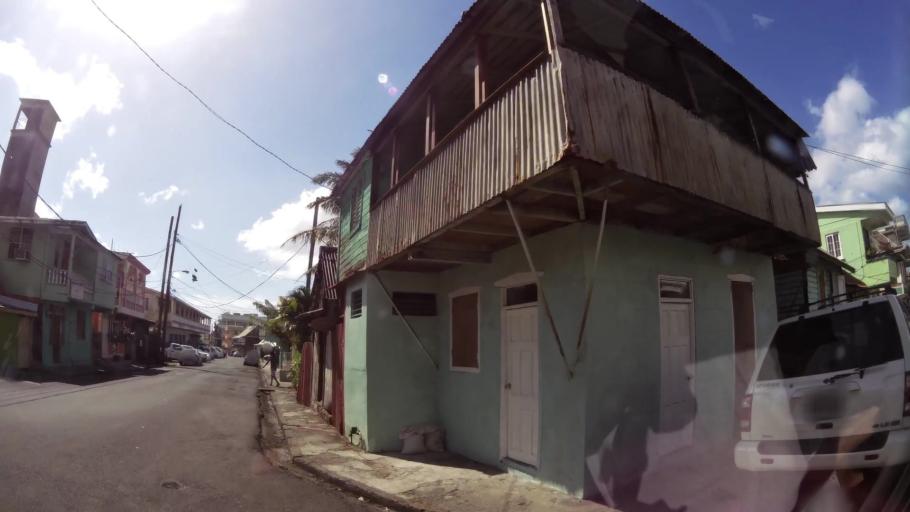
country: DM
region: Saint George
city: Roseau
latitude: 15.3006
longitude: -61.3850
